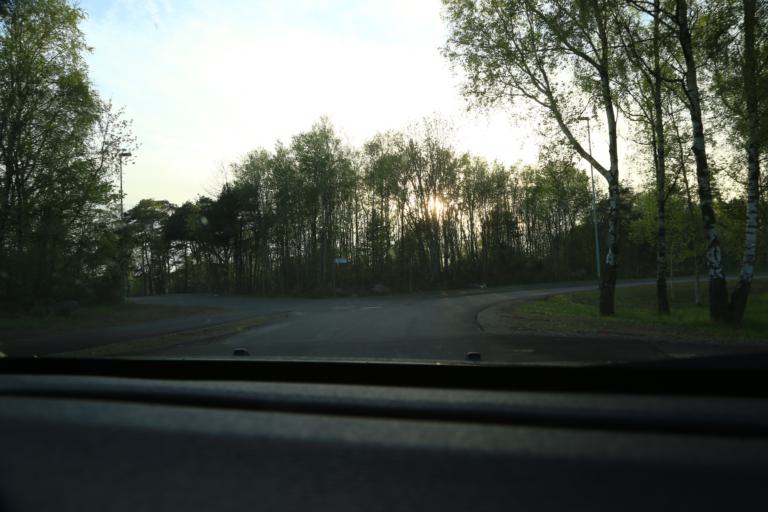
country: SE
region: Halland
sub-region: Varbergs Kommun
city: Traslovslage
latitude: 57.0634
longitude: 12.2853
